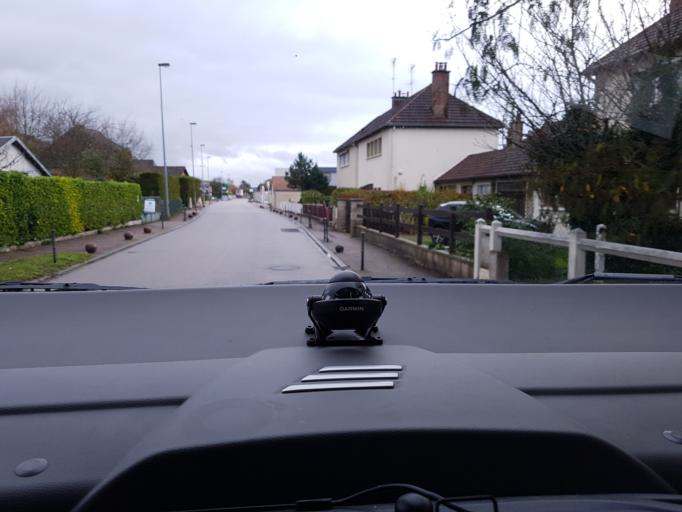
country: FR
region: Haute-Normandie
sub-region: Departement de l'Eure
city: Igoville
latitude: 49.3188
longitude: 1.1532
